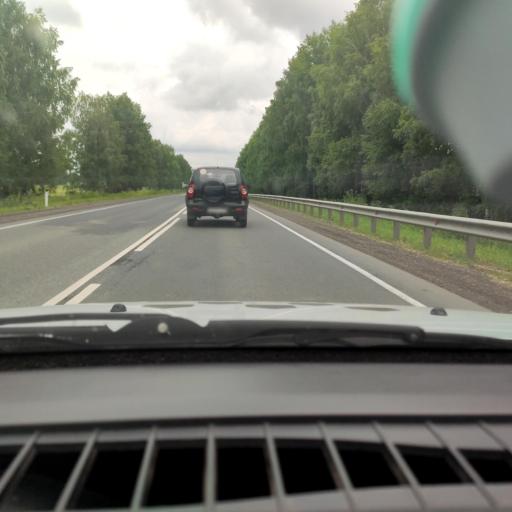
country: RU
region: Perm
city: Kukushtan
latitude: 57.4828
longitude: 56.6836
